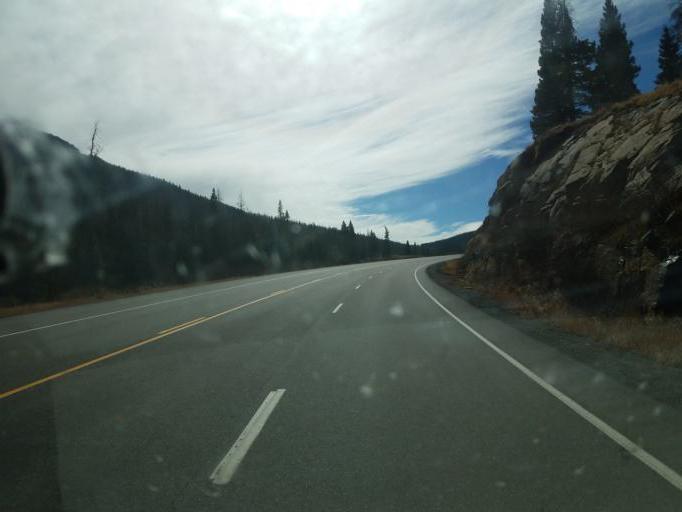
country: US
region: Colorado
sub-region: Archuleta County
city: Pagosa Springs
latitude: 37.5250
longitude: -106.7696
